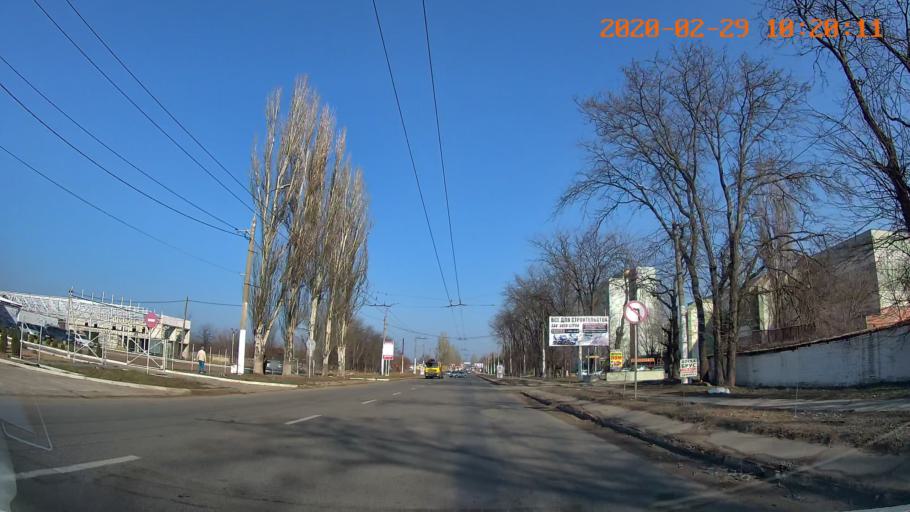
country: MD
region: Telenesti
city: Tiraspolul Nou
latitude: 46.8580
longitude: 29.6111
